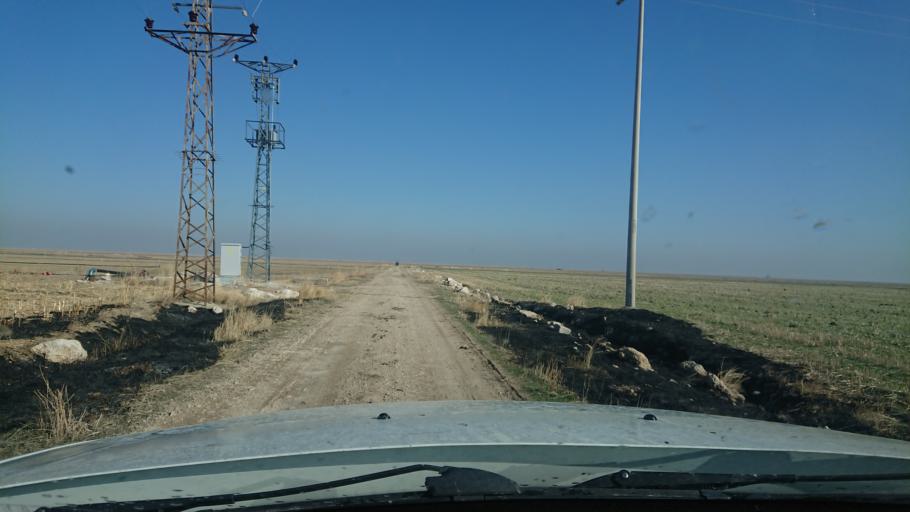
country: TR
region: Aksaray
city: Sultanhani
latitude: 38.3108
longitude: 33.5234
